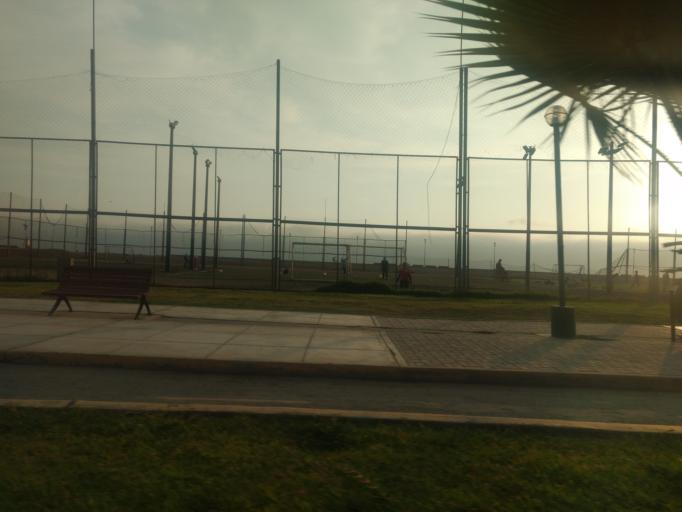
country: PE
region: Lima
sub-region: Lima
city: San Isidro
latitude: -12.1051
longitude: -77.0625
